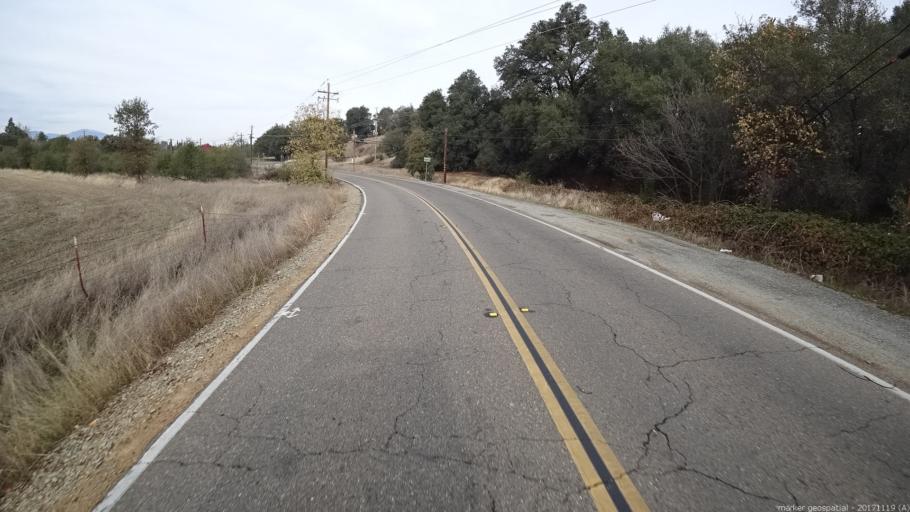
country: US
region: California
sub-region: Shasta County
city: Redding
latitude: 40.5342
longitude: -122.3341
